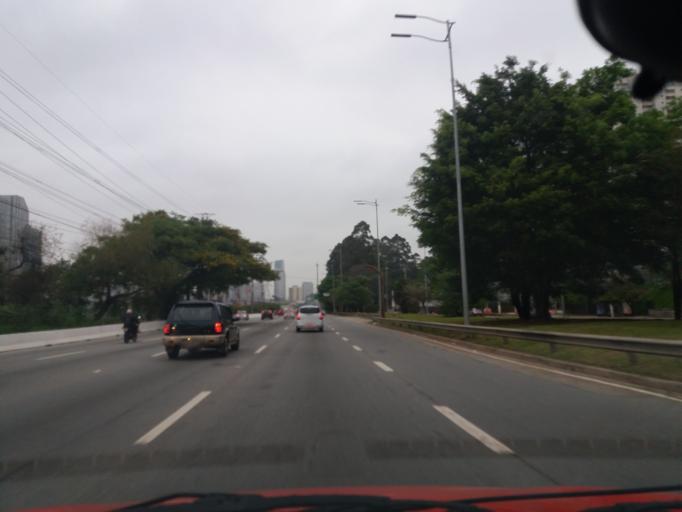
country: BR
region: Sao Paulo
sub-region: Sao Paulo
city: Sao Paulo
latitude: -23.6043
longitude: -46.6984
